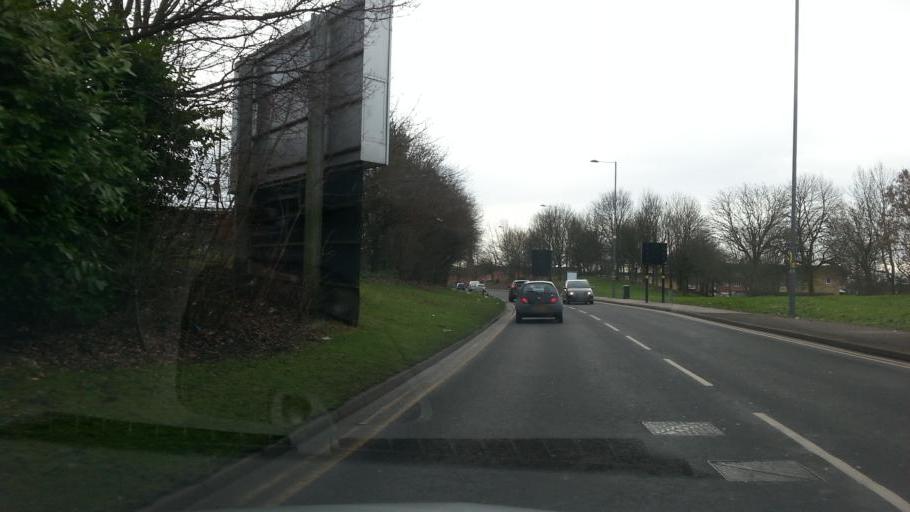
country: GB
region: England
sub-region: City and Borough of Birmingham
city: Birmingham
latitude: 52.4616
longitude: -1.8872
